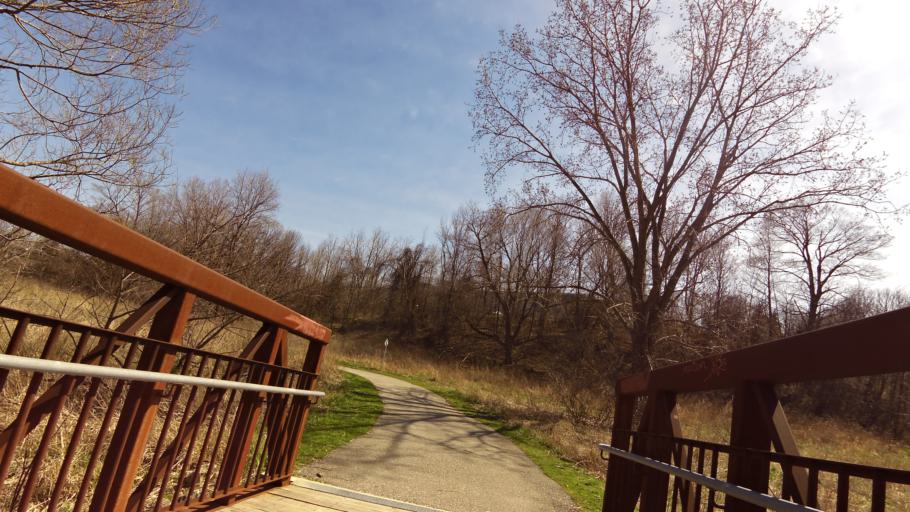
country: CA
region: Ontario
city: Etobicoke
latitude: 43.6526
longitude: -79.6198
